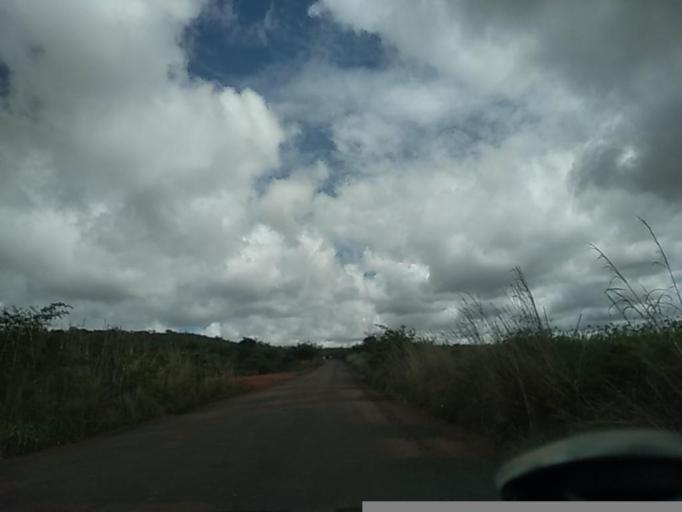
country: BR
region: Bahia
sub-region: Caetite
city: Caetite
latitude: -14.0333
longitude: -42.4869
